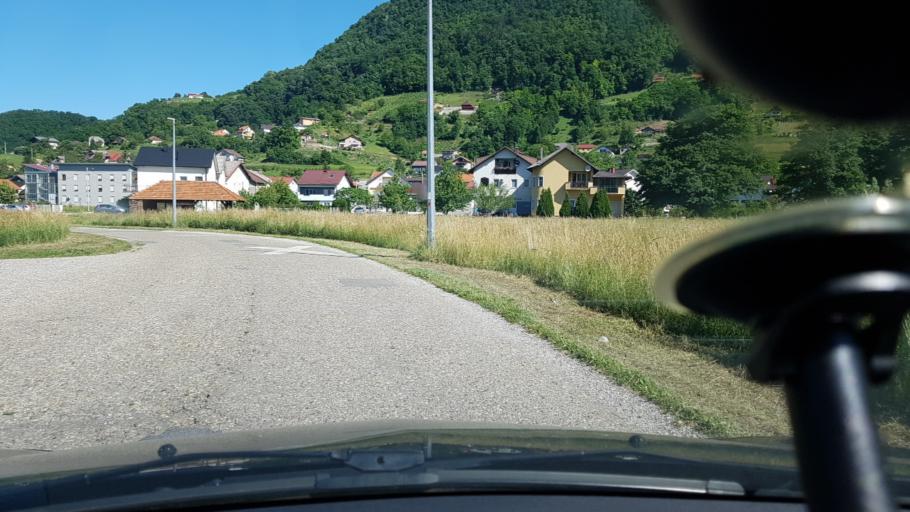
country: HR
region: Krapinsko-Zagorska
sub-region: Grad Krapina
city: Krapina
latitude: 46.1788
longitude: 15.8659
